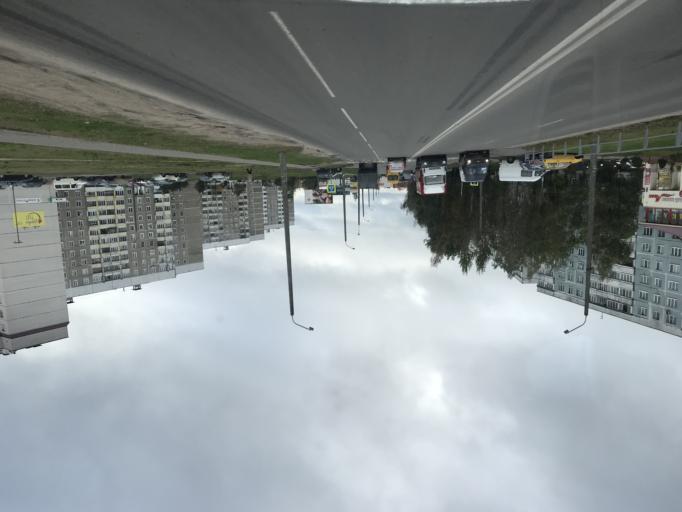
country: BY
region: Mogilev
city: Mahilyow
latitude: 53.8764
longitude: 30.3668
